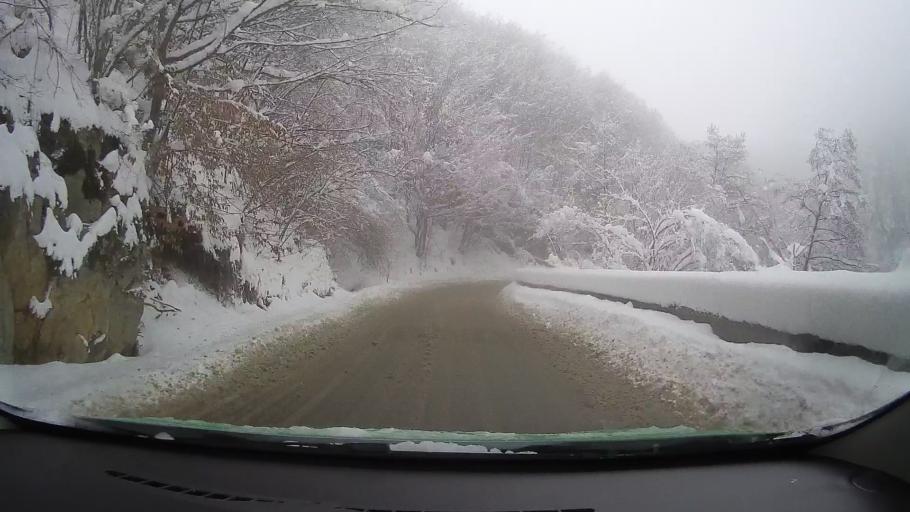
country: RO
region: Sibiu
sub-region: Comuna Tilisca
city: Tilisca
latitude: 45.8002
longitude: 23.7953
